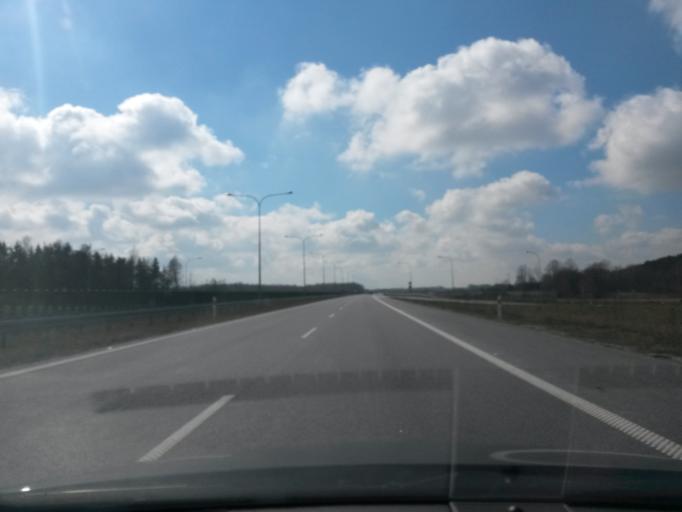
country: PL
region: Lodz Voivodeship
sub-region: powiat Lowicki
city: Bobrowniki
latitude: 52.0276
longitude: 20.0023
